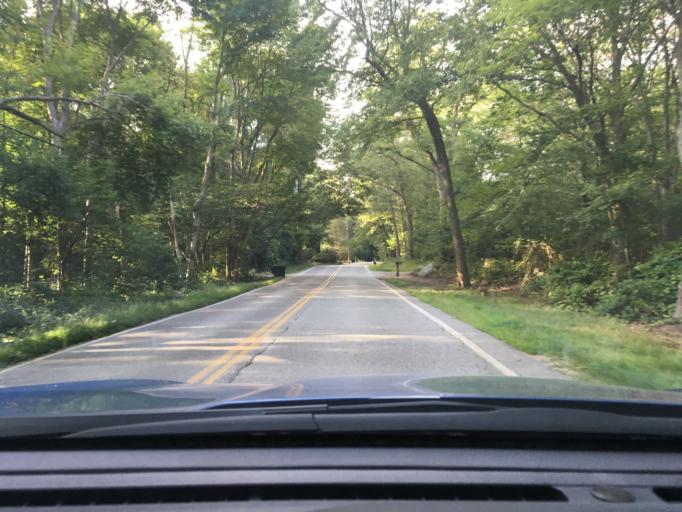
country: US
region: Rhode Island
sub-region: Kent County
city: West Warwick
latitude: 41.6361
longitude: -71.5148
